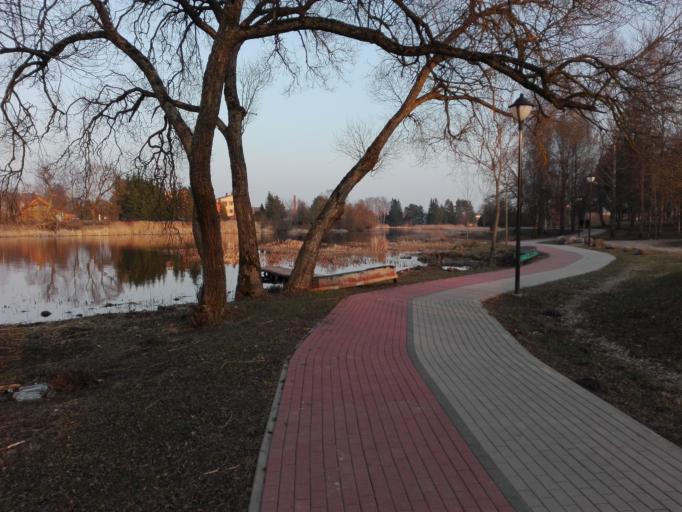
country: LT
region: Panevezys
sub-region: Birzai
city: Birzai
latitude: 56.2087
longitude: 24.7595
